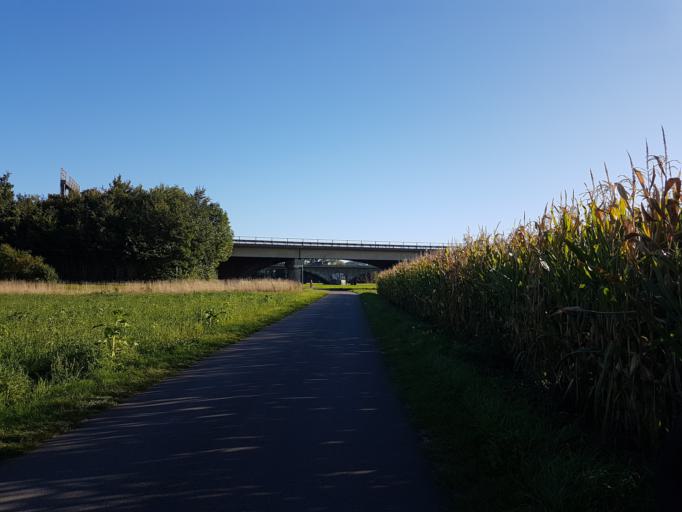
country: DE
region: North Rhine-Westphalia
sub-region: Regierungsbezirk Detmold
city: Vlotho
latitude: 52.2081
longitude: 8.8482
